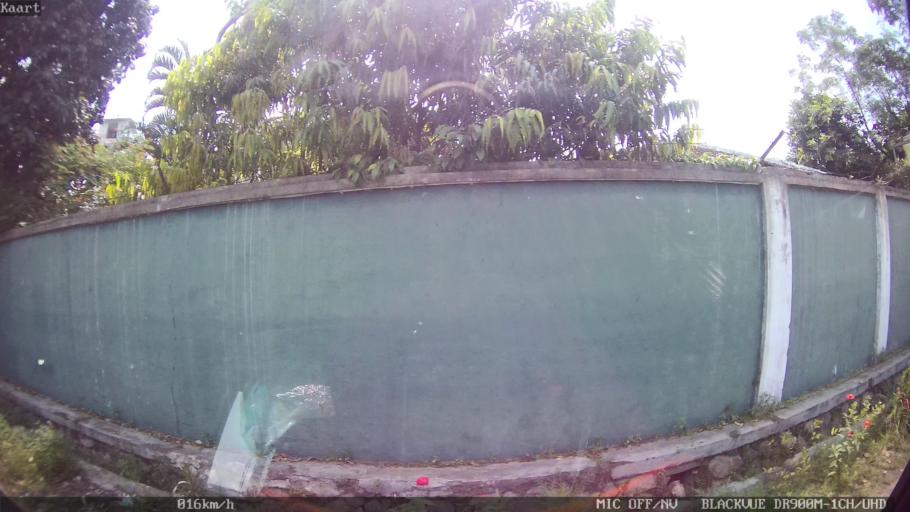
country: ID
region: Lampung
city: Pringsewu
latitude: -5.3579
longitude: 104.9758
